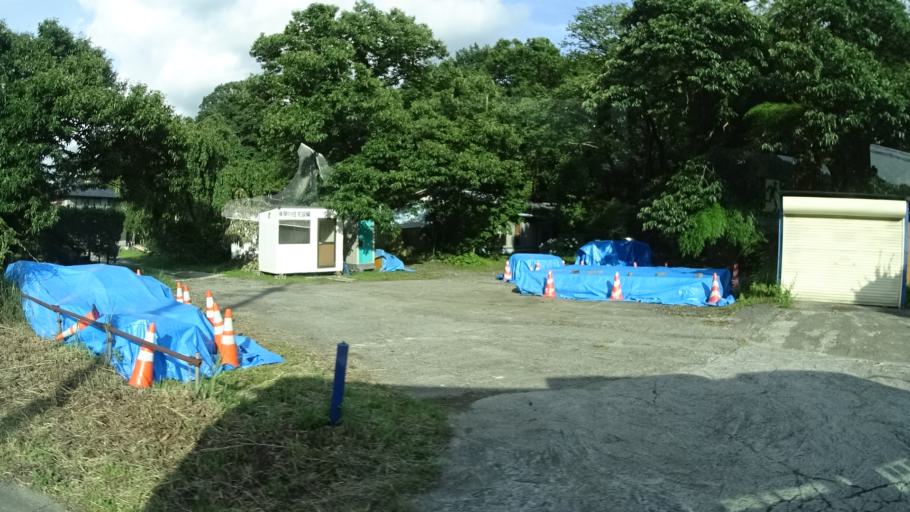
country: JP
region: Tochigi
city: Nikko
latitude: 36.6604
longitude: 139.4594
